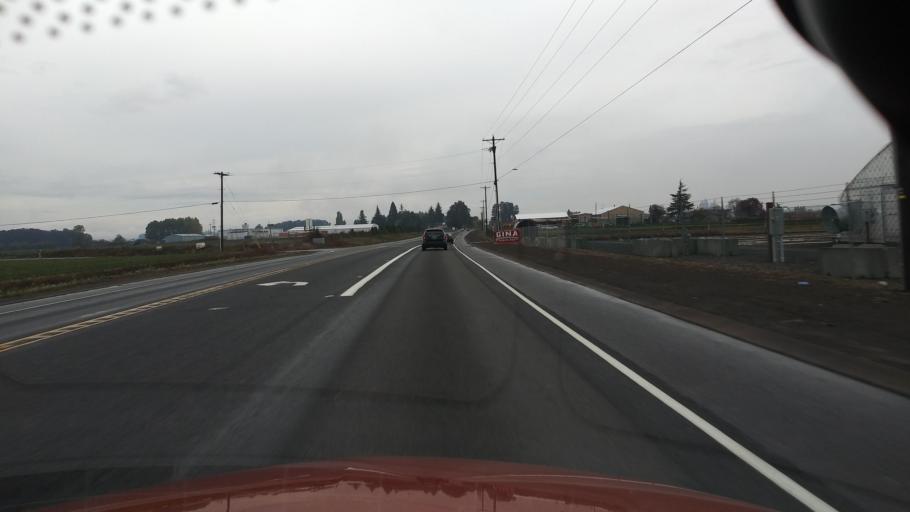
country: US
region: Oregon
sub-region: Washington County
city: Cornelius
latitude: 45.5655
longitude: -123.0519
